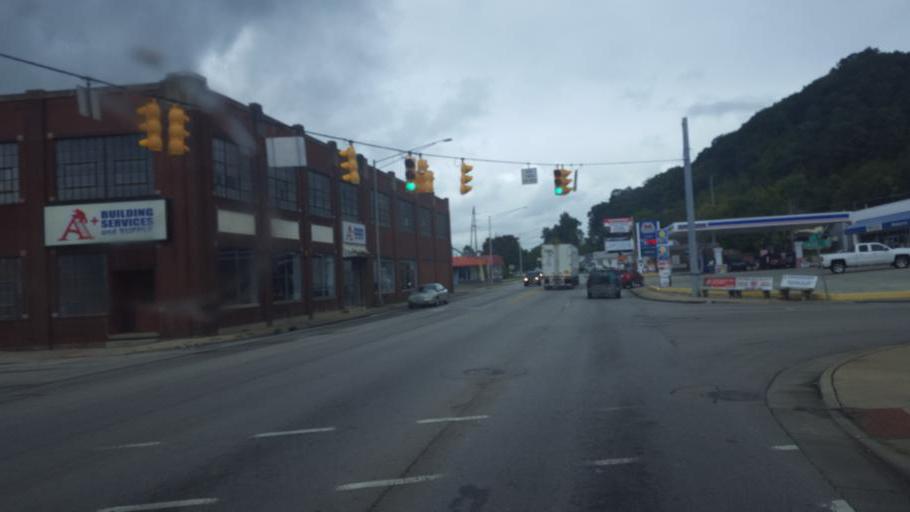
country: US
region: Ohio
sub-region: Scioto County
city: Portsmouth
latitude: 38.7589
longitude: -82.9906
